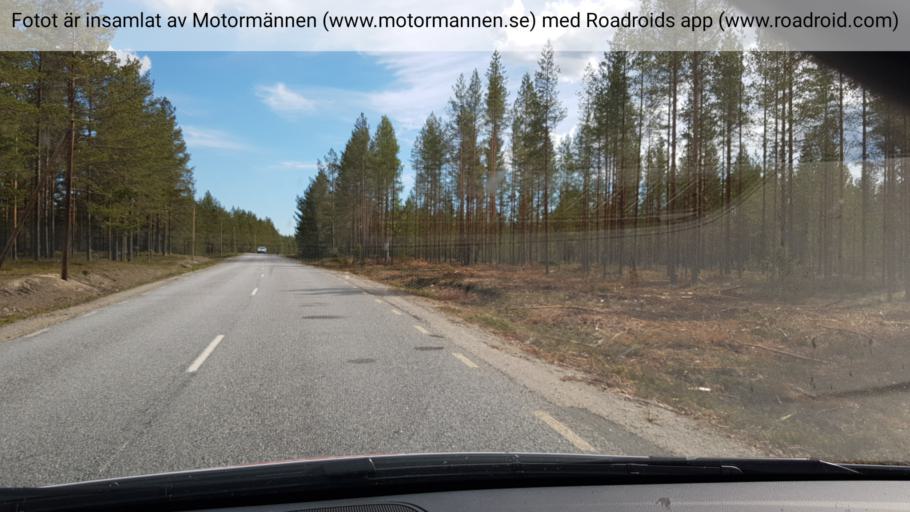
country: SE
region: Vaesterbotten
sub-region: Umea Kommun
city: Saevar
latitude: 64.0140
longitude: 20.4893
